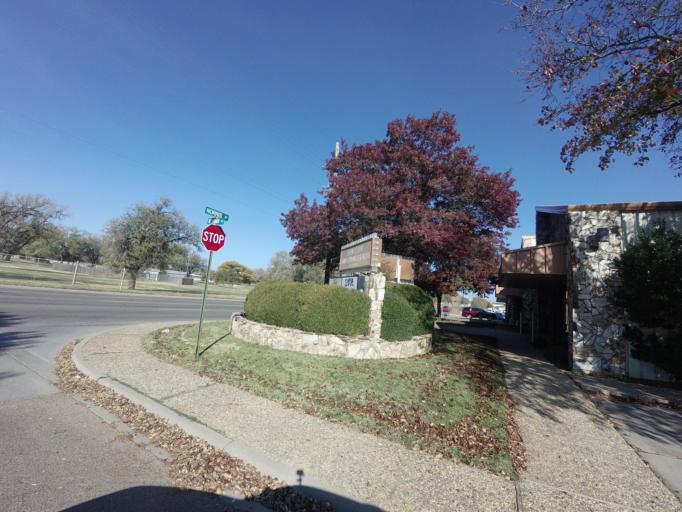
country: US
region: New Mexico
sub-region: Curry County
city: Clovis
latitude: 34.4068
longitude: -103.1787
